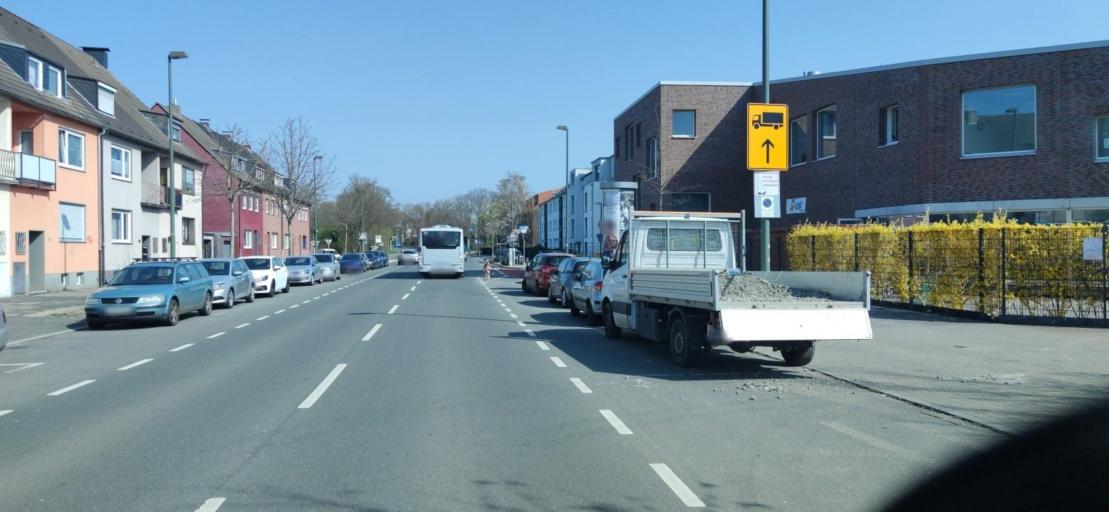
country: DE
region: North Rhine-Westphalia
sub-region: Regierungsbezirk Dusseldorf
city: Dusseldorf
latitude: 51.1869
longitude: 6.8271
